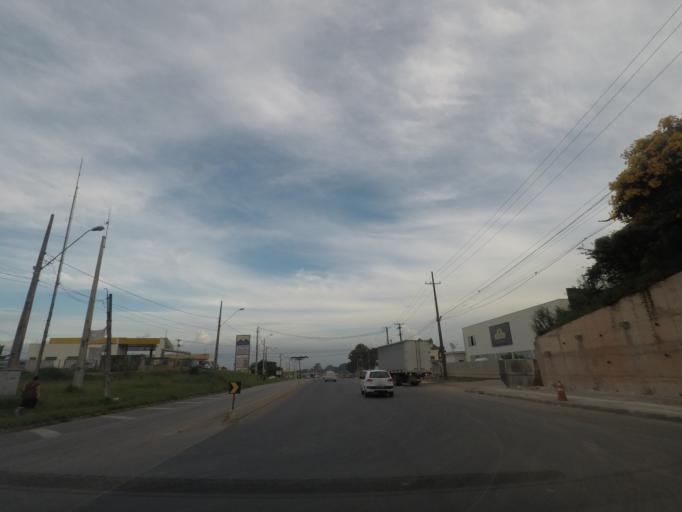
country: BR
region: Parana
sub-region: Colombo
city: Colombo
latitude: -25.3288
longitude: -49.2211
